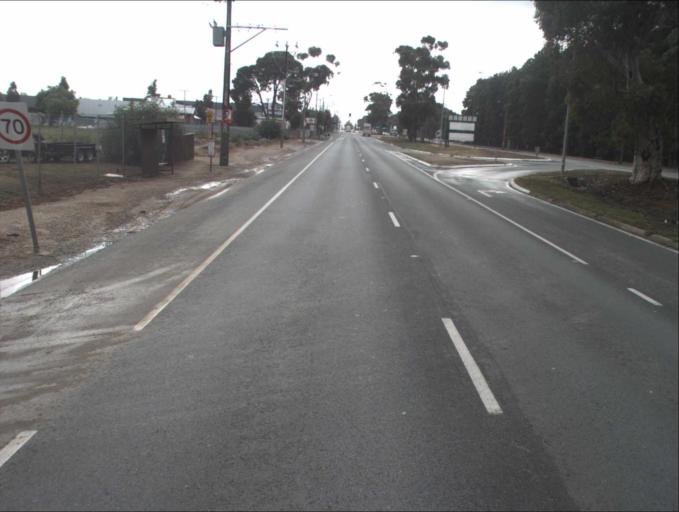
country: AU
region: South Australia
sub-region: Port Adelaide Enfield
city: Enfield
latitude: -34.8416
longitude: 138.6048
